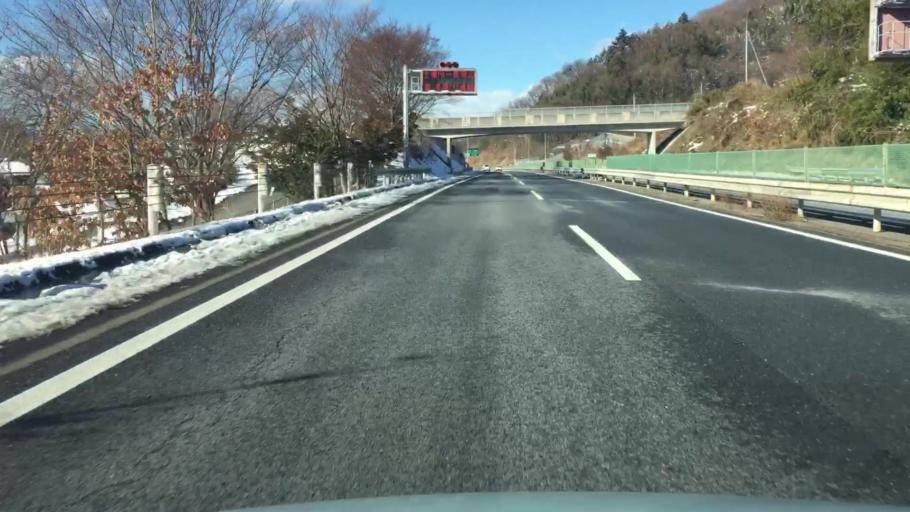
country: JP
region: Gunma
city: Numata
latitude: 36.6742
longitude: 139.0297
